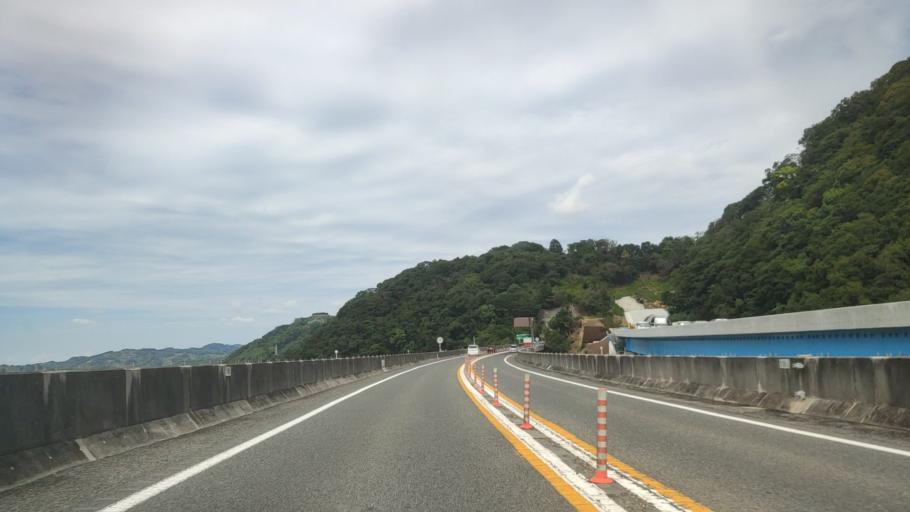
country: JP
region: Wakayama
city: Gobo
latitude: 34.0125
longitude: 135.1898
